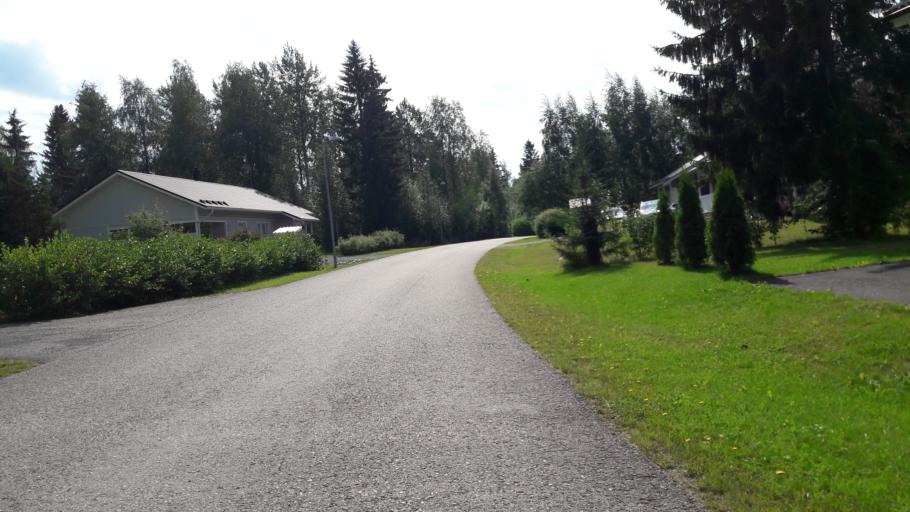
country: FI
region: North Karelia
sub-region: Joensuu
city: Joensuu
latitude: 62.5088
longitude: 29.8283
